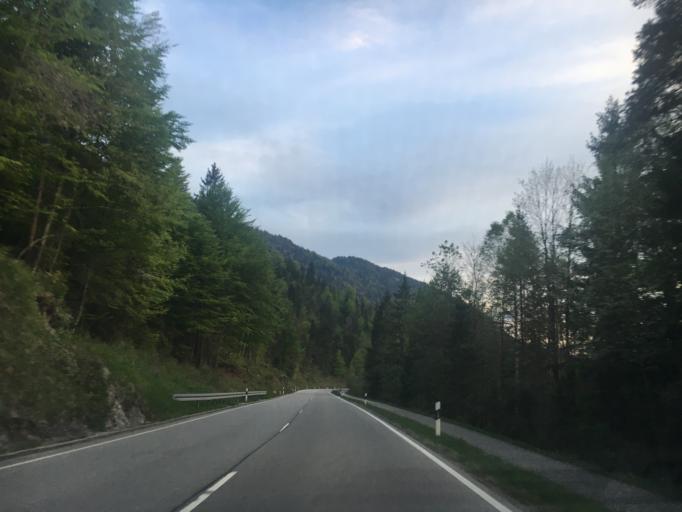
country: DE
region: Bavaria
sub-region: Upper Bavaria
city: Lenggries
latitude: 47.6156
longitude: 11.5888
